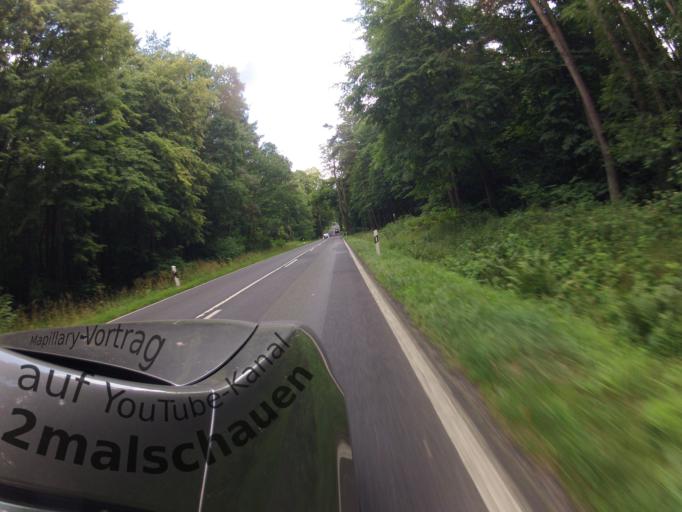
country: DE
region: Mecklenburg-Vorpommern
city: Usedom
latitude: 53.9071
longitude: 14.0281
